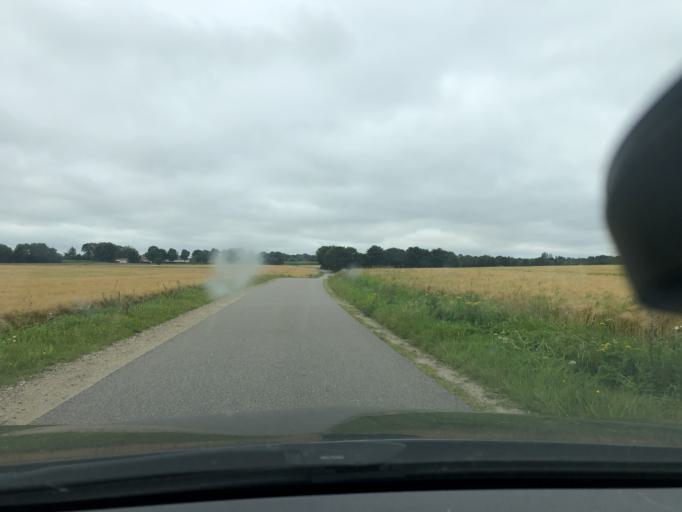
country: DK
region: South Denmark
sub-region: Varde Kommune
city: Olgod
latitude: 55.8061
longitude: 8.5970
